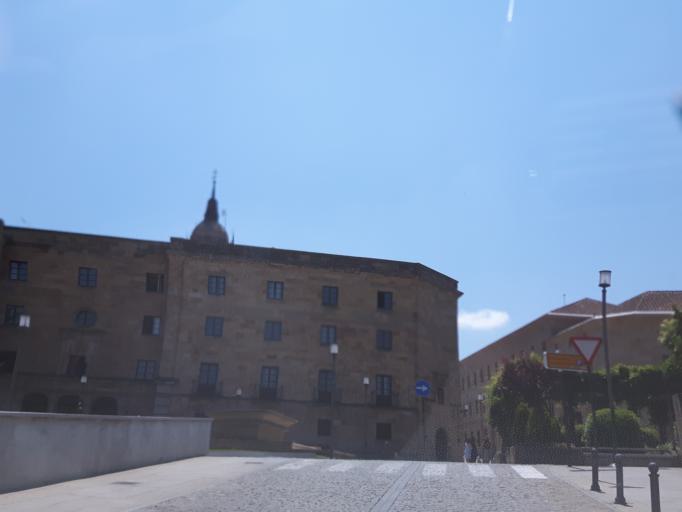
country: ES
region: Castille and Leon
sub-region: Provincia de Salamanca
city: Salamanca
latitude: 40.9618
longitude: -5.6693
